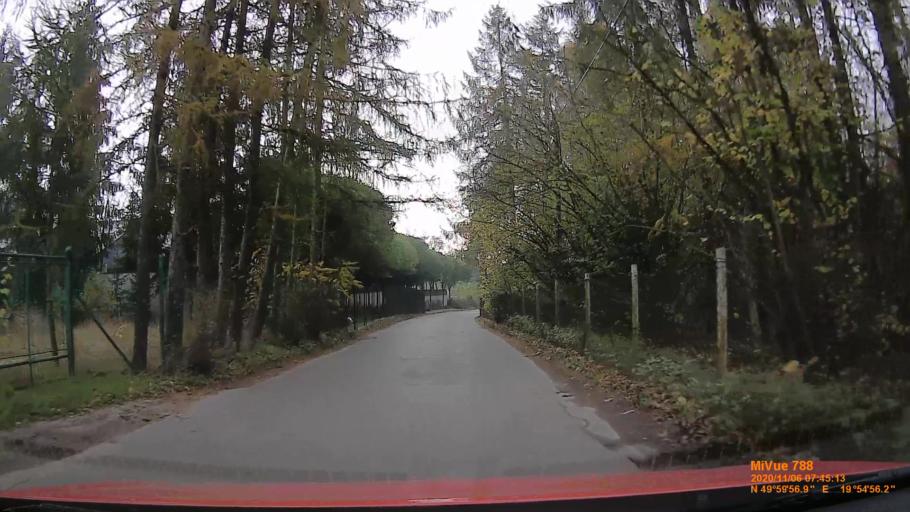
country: PL
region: Lesser Poland Voivodeship
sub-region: Powiat krakowski
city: Libertow
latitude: 49.9991
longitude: 19.9156
